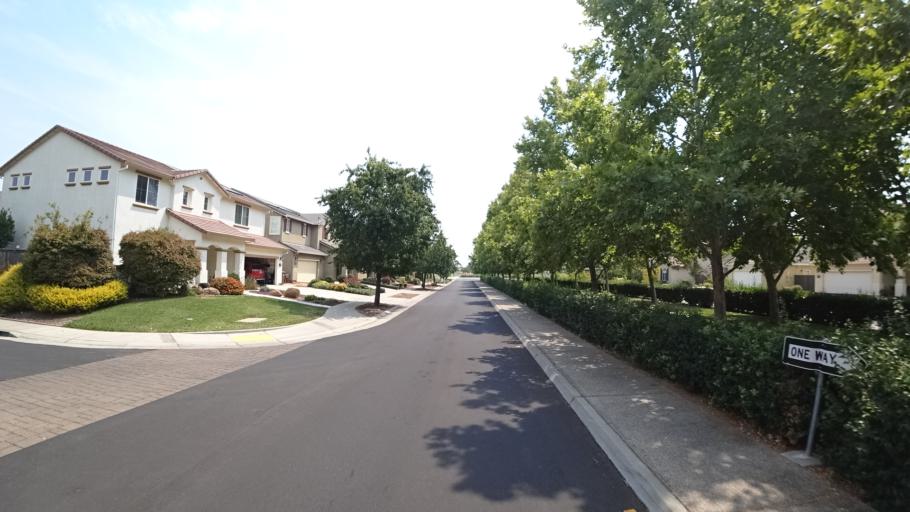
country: US
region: California
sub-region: Sacramento County
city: Laguna
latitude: 38.4021
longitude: -121.4096
